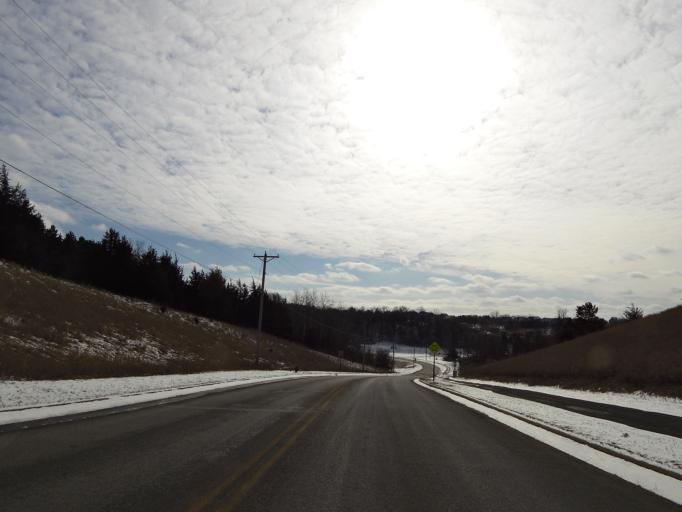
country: US
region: Minnesota
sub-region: Hennepin County
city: Eden Prairie
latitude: 44.8317
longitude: -93.4837
